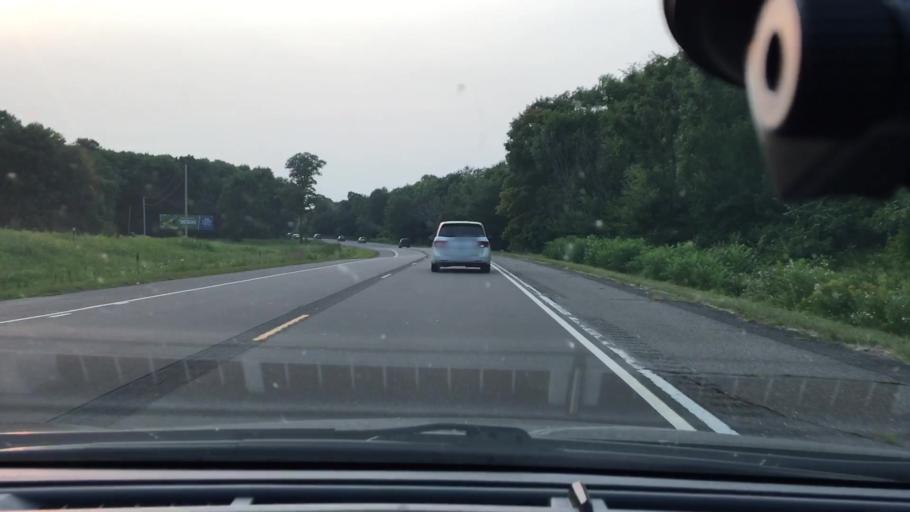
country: US
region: Minnesota
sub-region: Mille Lacs County
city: Vineland
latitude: 46.1422
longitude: -93.7085
